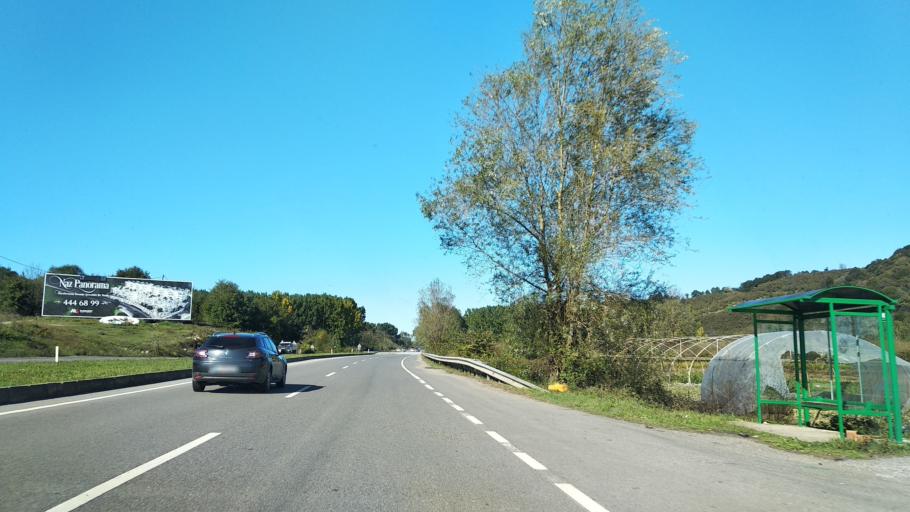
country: TR
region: Sakarya
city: Karasu
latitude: 41.0550
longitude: 30.6358
